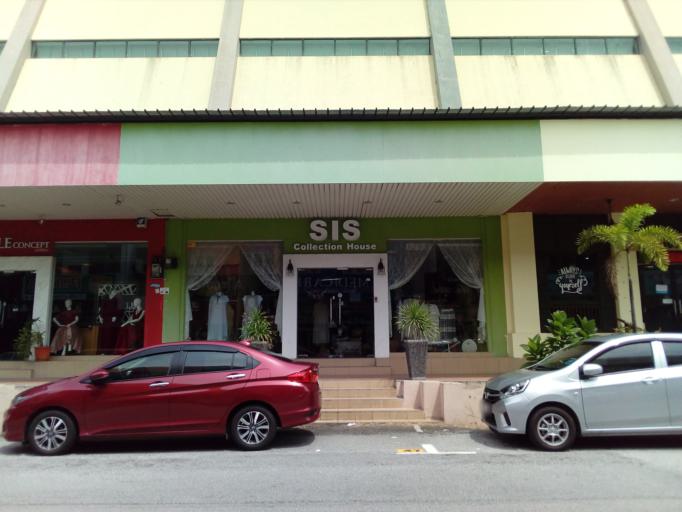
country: MY
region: Perak
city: Ipoh
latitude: 4.6071
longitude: 101.1190
